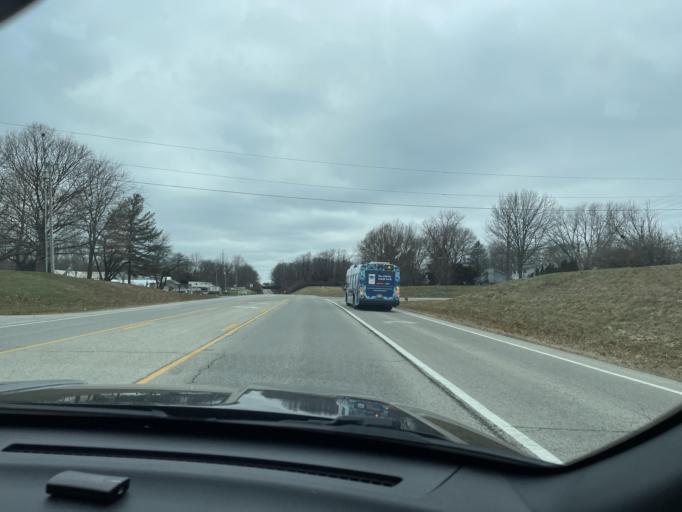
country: US
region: Illinois
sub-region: Sangamon County
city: Leland Grove
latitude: 39.8176
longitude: -89.7065
